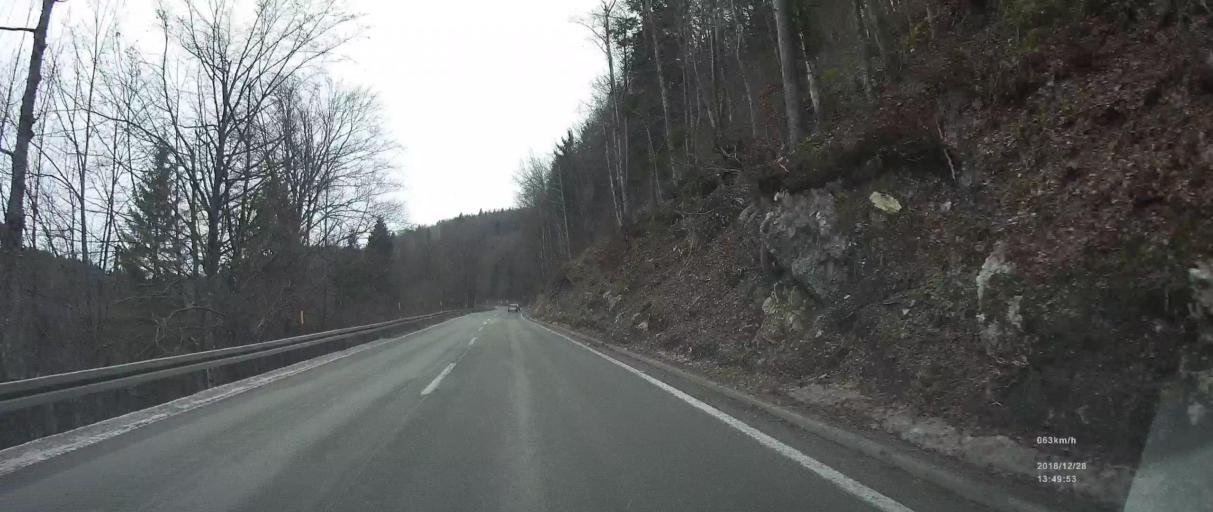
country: HR
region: Primorsko-Goranska
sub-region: Grad Delnice
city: Delnice
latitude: 45.3974
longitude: 14.8238
